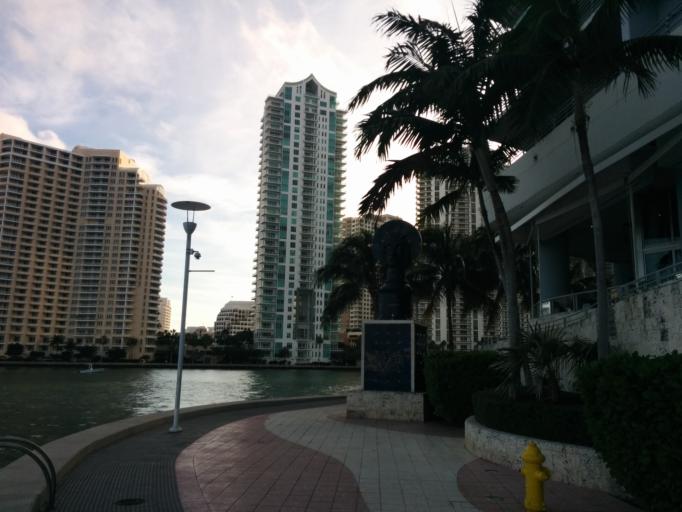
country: US
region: Florida
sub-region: Miami-Dade County
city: Miami
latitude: 25.7719
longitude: -80.1851
